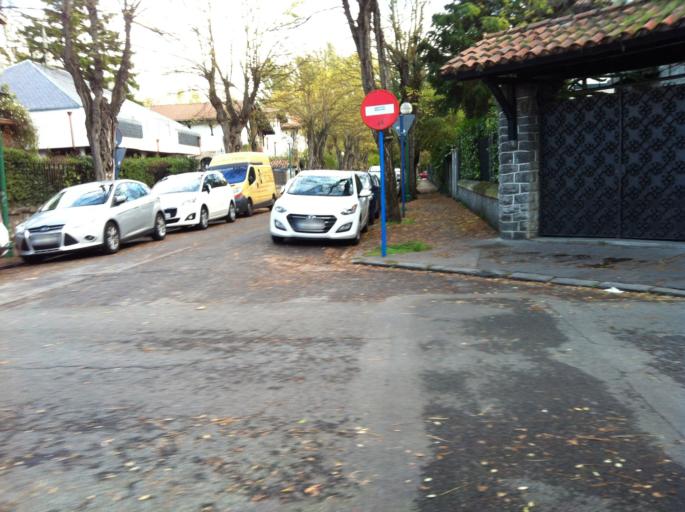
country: ES
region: Basque Country
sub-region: Provincia de Alava
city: Gasteiz / Vitoria
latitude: 42.8381
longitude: -2.6767
